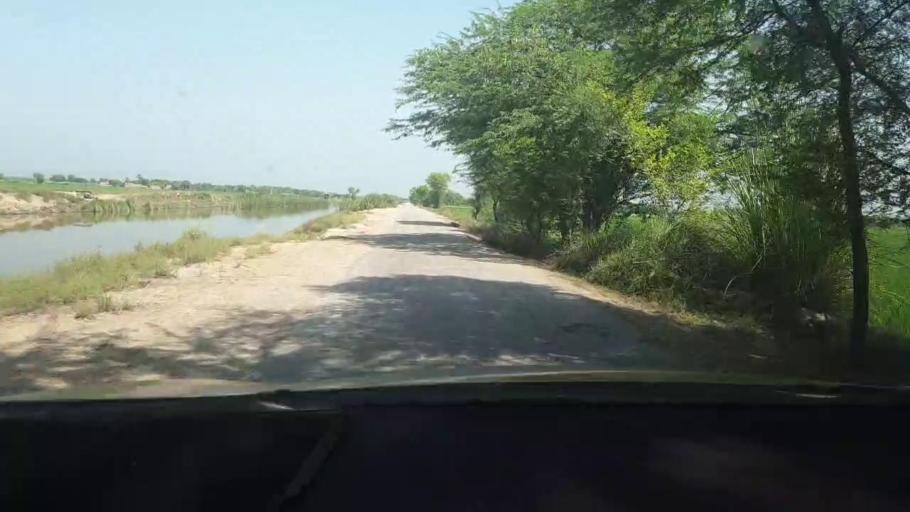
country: PK
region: Sindh
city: Miro Khan
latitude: 27.7060
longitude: 68.0730
